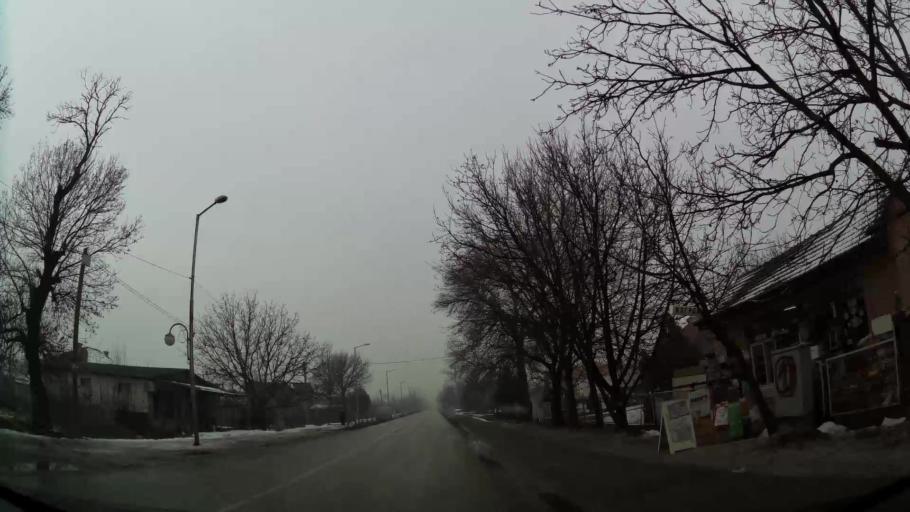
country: MK
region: Petrovec
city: Petrovec
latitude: 41.9338
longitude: 21.6219
